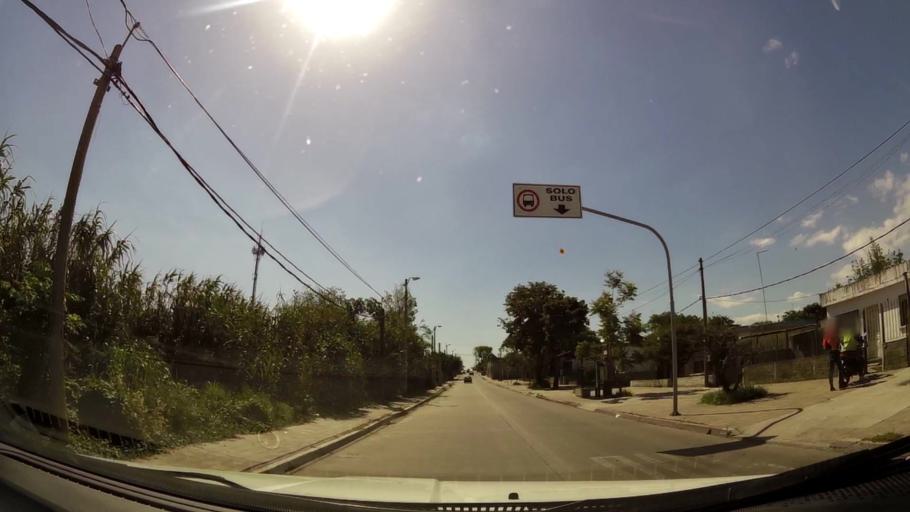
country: UY
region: Montevideo
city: Montevideo
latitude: -34.8458
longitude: -56.2364
